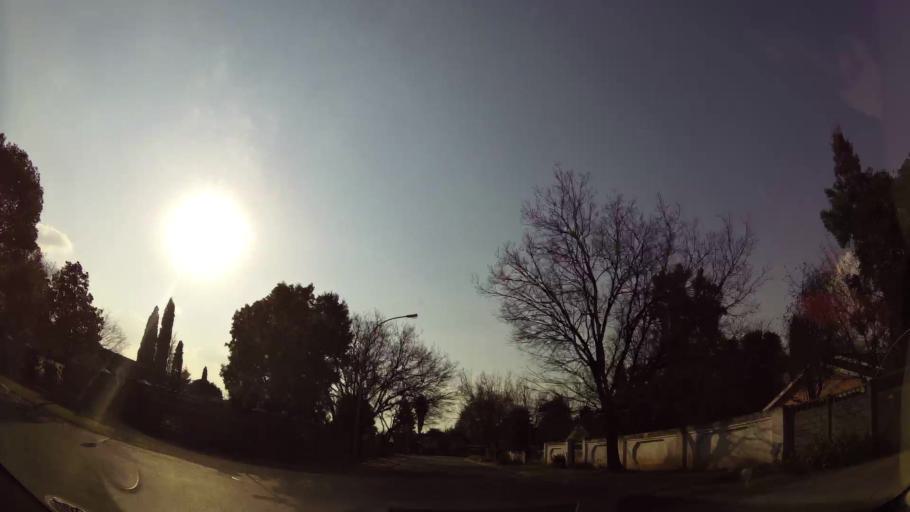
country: ZA
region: Gauteng
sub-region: Ekurhuleni Metropolitan Municipality
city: Benoni
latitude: -26.1268
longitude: 28.3709
